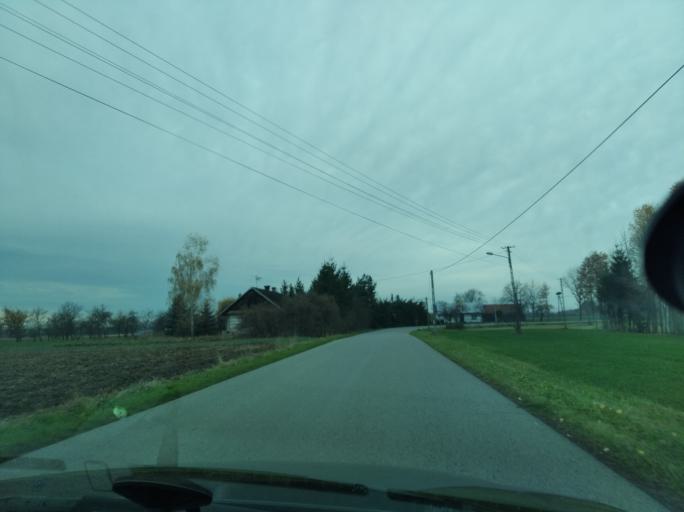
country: PL
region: Subcarpathian Voivodeship
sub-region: Powiat przeworski
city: Nowosielce
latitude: 50.0936
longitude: 22.4101
